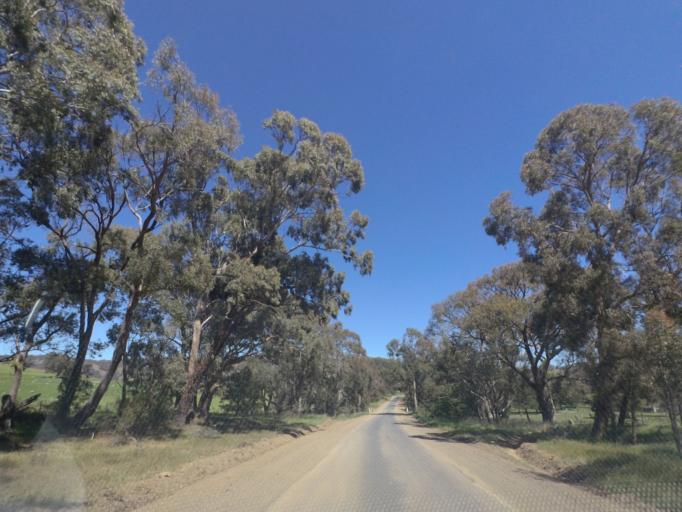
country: AU
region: Victoria
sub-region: Whittlesea
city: Whittlesea
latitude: -37.2896
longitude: 144.9913
